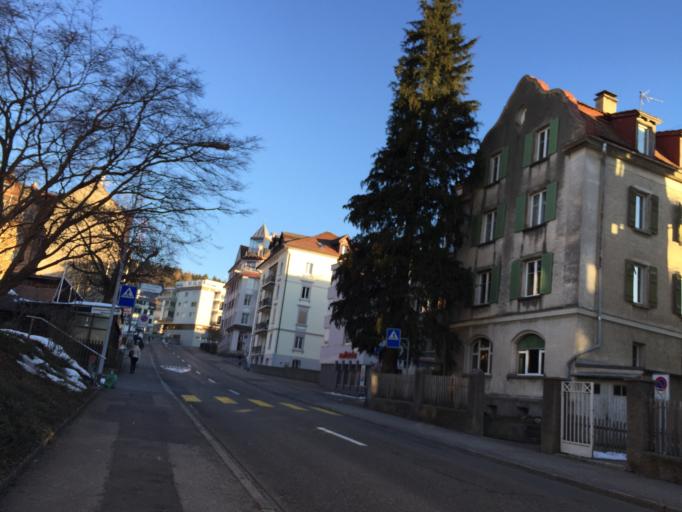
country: CH
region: Saint Gallen
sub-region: Wahlkreis St. Gallen
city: Sankt Gallen
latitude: 47.4399
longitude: 9.3943
